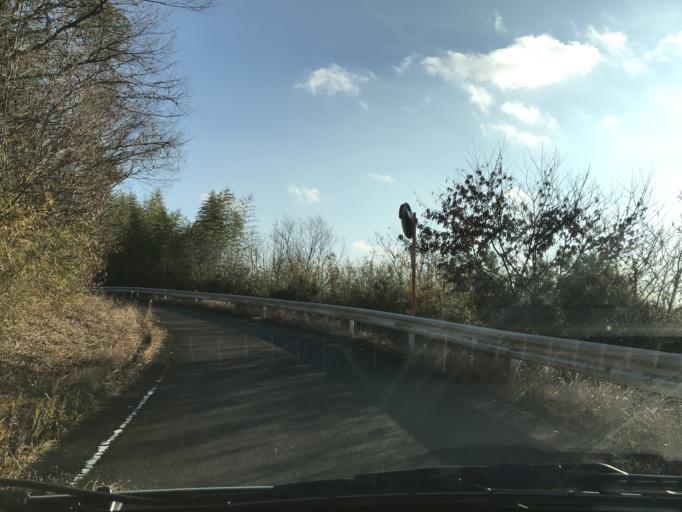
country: JP
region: Miyagi
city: Wakuya
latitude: 38.6933
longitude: 141.1138
